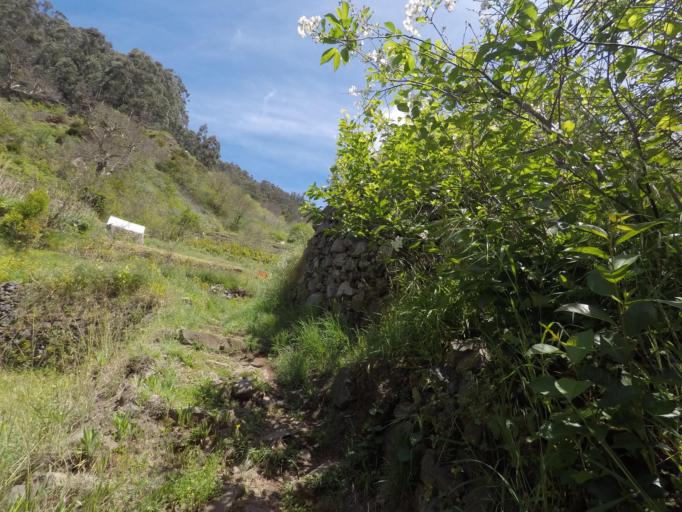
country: PT
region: Madeira
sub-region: Camara de Lobos
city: Curral das Freiras
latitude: 32.7437
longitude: -16.9673
